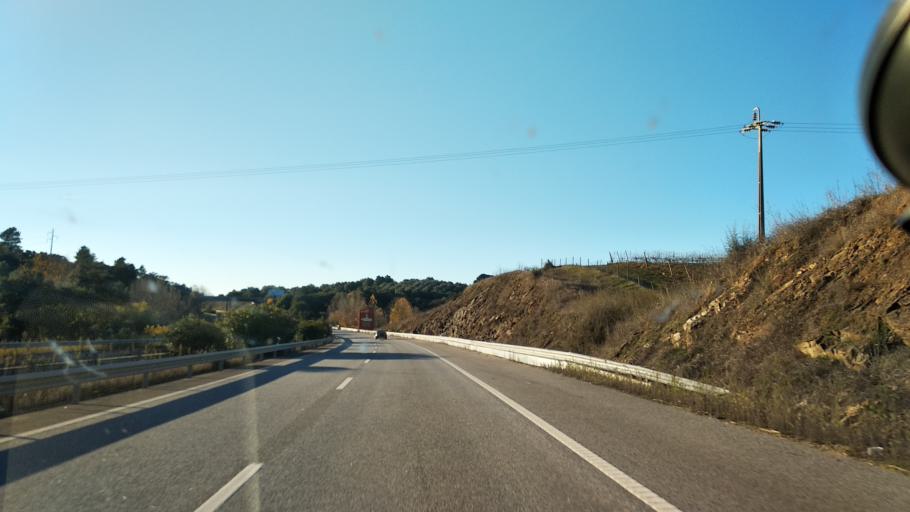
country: PT
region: Santarem
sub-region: Abrantes
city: Alferrarede
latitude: 39.4862
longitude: -8.1486
